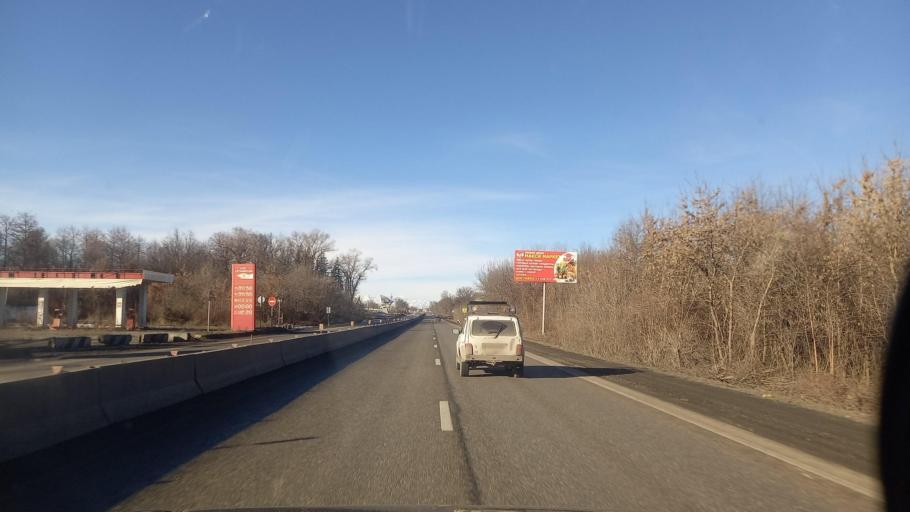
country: RU
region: North Ossetia
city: Gizel'
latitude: 43.0286
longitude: 44.5903
